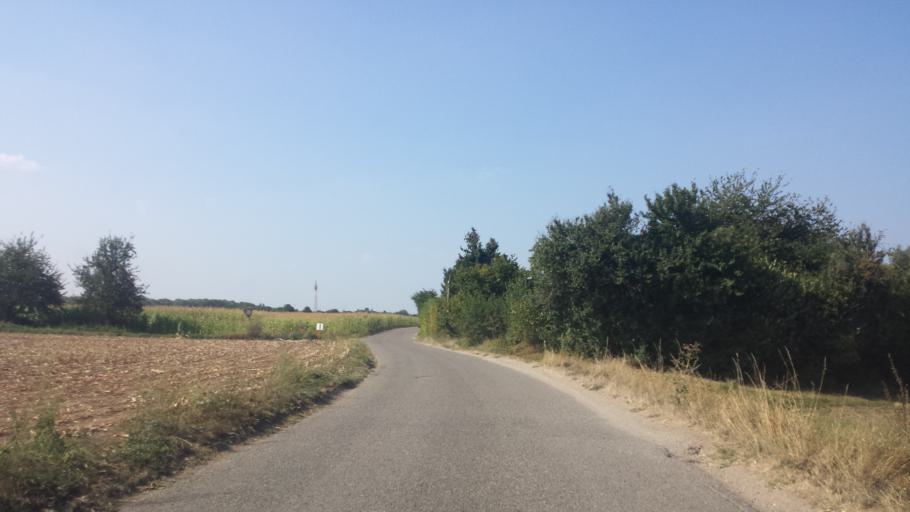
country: DE
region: Baden-Wuerttemberg
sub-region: Karlsruhe Region
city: Edingen-Neckarhausen
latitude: 49.4583
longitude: 8.6247
